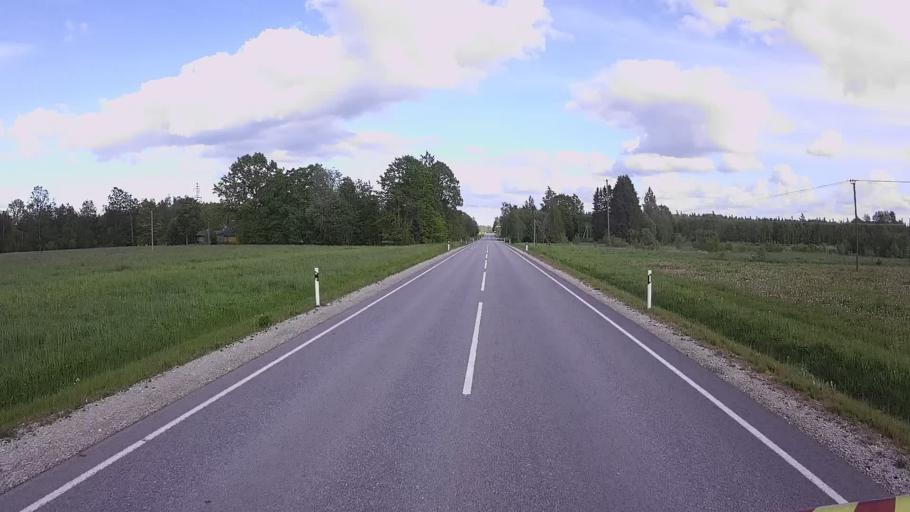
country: EE
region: Jogevamaa
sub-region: Mustvee linn
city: Mustvee
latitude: 58.8693
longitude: 26.8291
